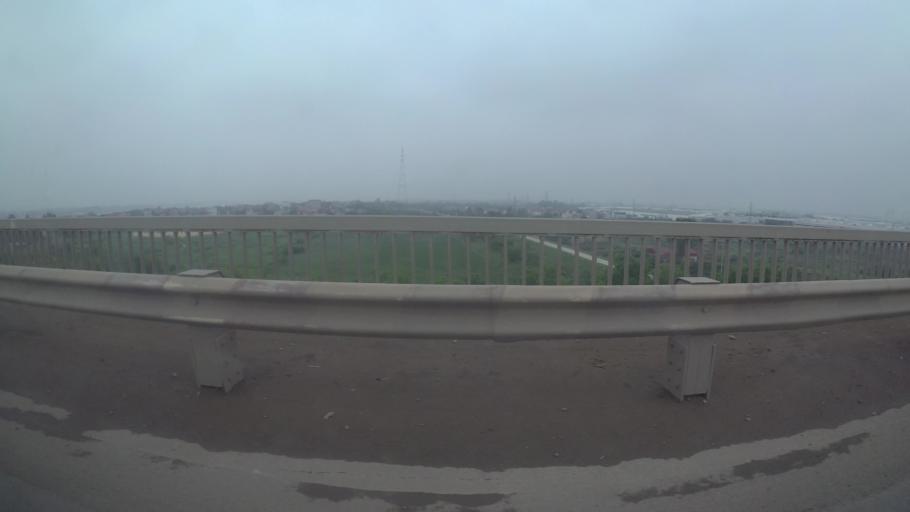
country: VN
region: Ha Noi
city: Tay Ho
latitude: 21.1060
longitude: 105.7871
